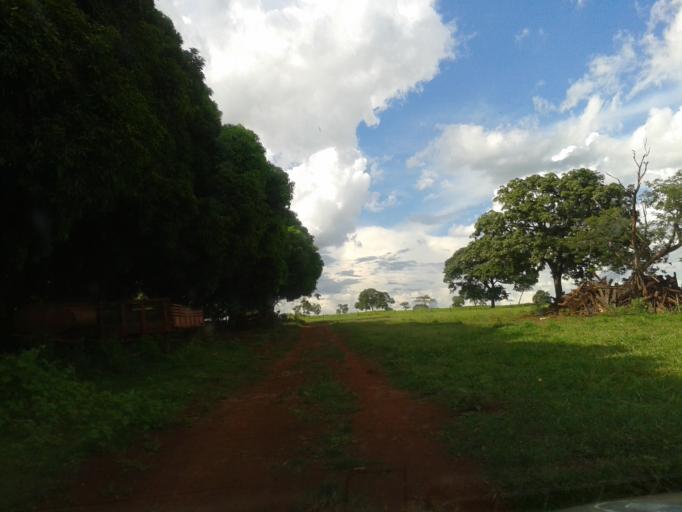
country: BR
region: Minas Gerais
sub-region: Capinopolis
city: Capinopolis
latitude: -18.7641
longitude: -49.8249
